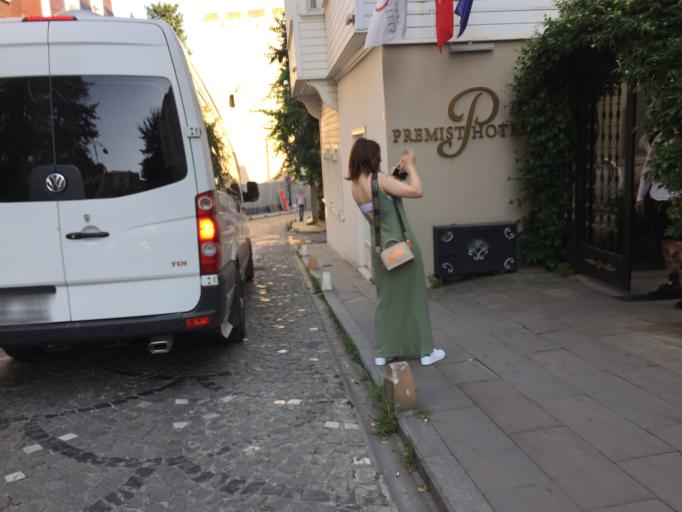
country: TR
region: Istanbul
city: Eminoenue
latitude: 41.0063
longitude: 28.9819
